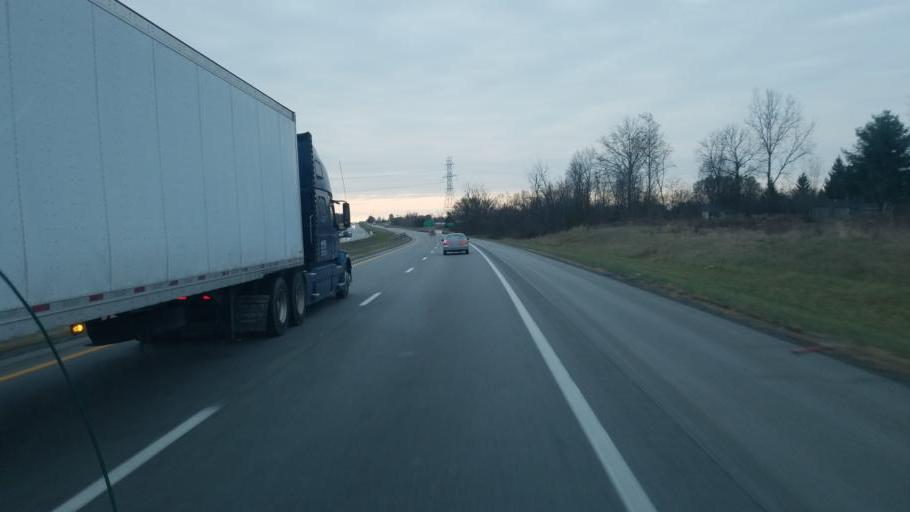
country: US
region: Ohio
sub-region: Allen County
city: Fort Shawnee
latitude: 40.6746
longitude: -84.1314
